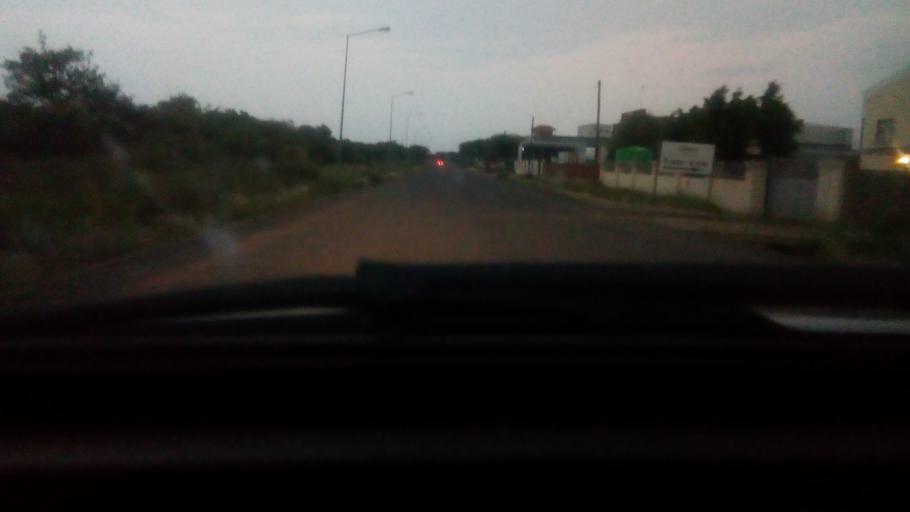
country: BW
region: Kweneng
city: Mmopone
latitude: -24.5925
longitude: 25.9100
